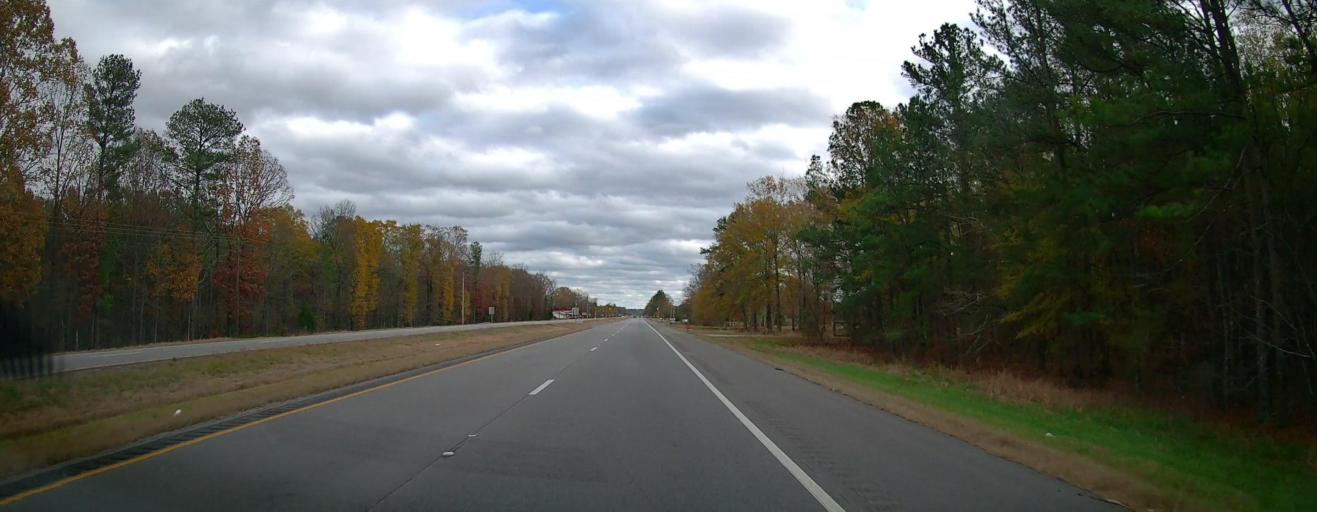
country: US
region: Alabama
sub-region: Lawrence County
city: Town Creek
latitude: 34.6564
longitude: -87.5346
